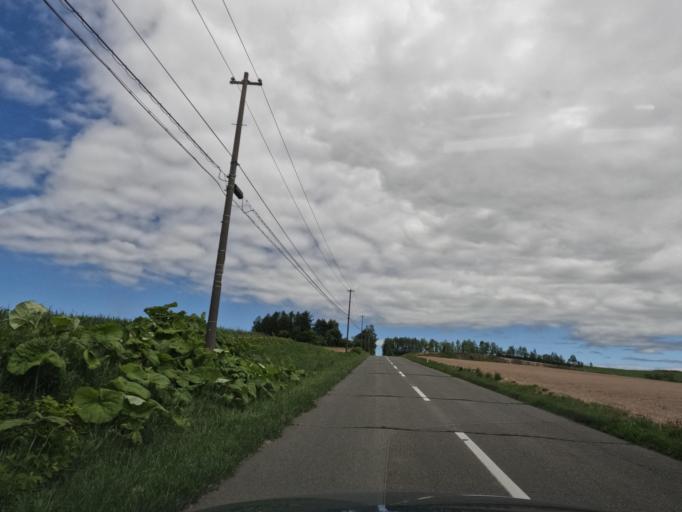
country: JP
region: Hokkaido
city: Shimo-furano
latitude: 43.5161
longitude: 142.4265
